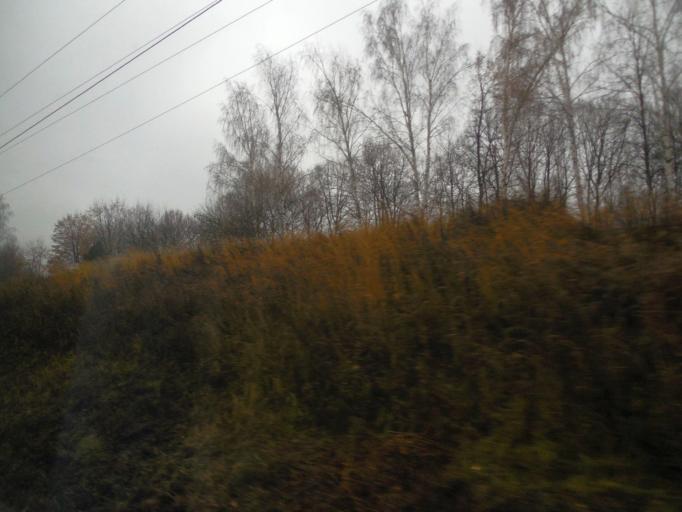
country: RU
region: Moskovskaya
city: Vostryakovo
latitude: 55.3860
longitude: 37.8120
